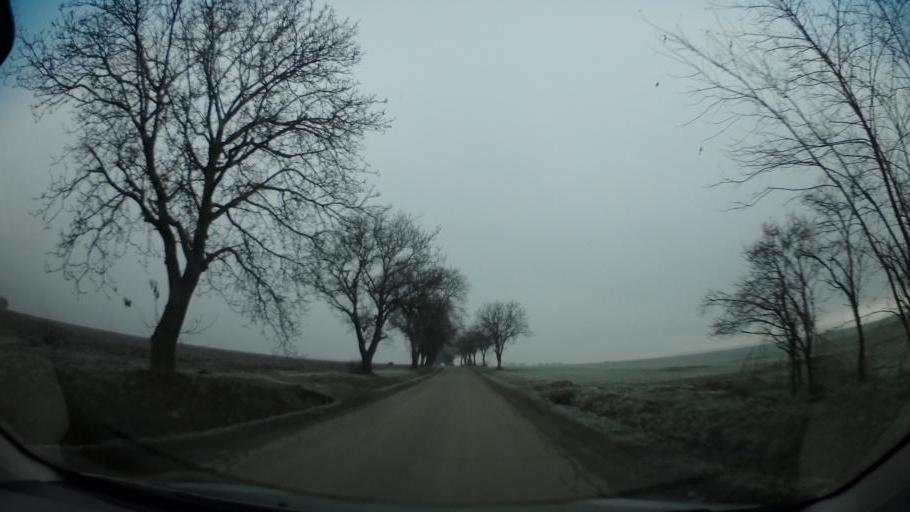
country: CZ
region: Vysocina
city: Mohelno
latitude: 49.1202
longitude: 16.2125
